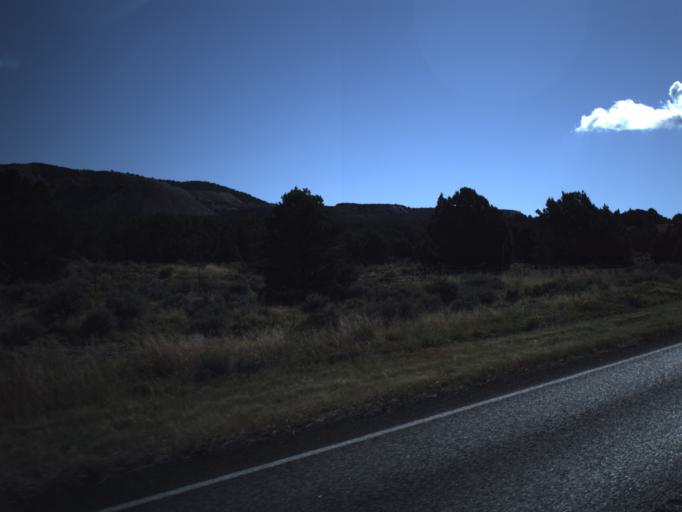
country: US
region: Utah
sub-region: Washington County
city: Enterprise
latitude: 37.6242
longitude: -113.4189
